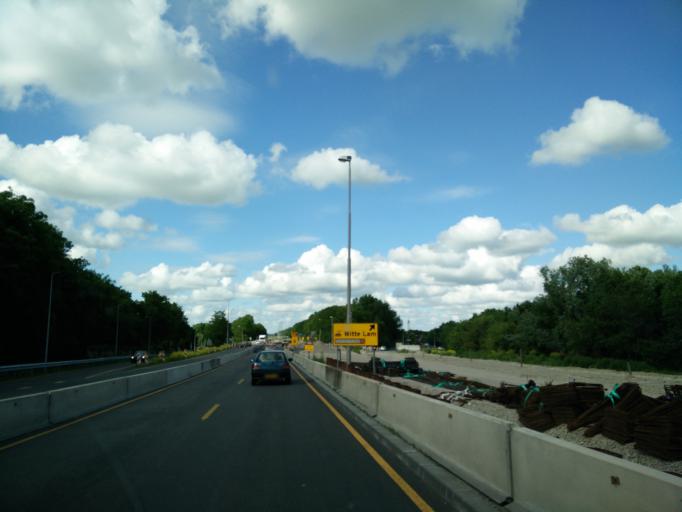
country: NL
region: Groningen
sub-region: Gemeente Groningen
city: Korrewegwijk
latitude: 53.2406
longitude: 6.5685
